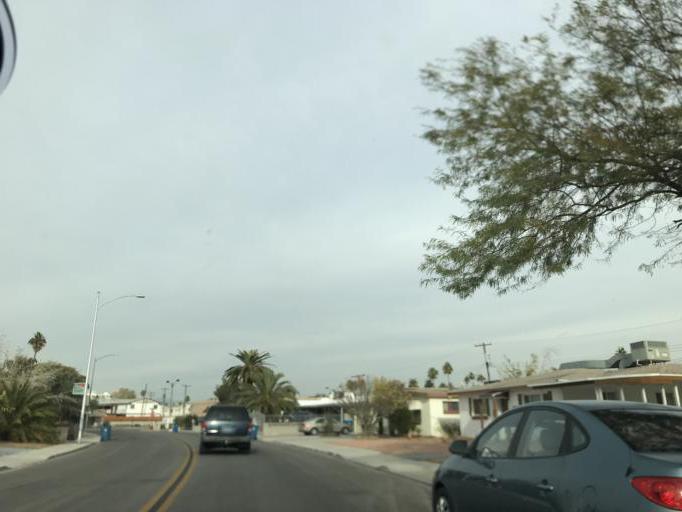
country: US
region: Nevada
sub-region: Clark County
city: Las Vegas
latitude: 36.1465
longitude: -115.1512
